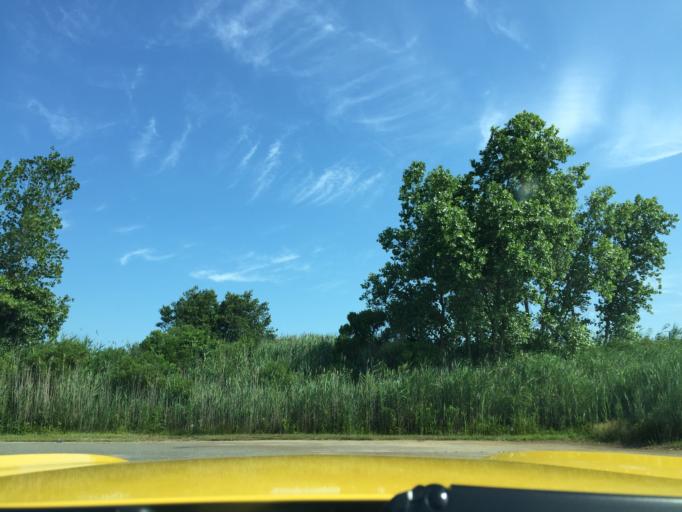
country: US
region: New York
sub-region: Suffolk County
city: Mastic Beach
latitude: 40.7415
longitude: -72.8723
